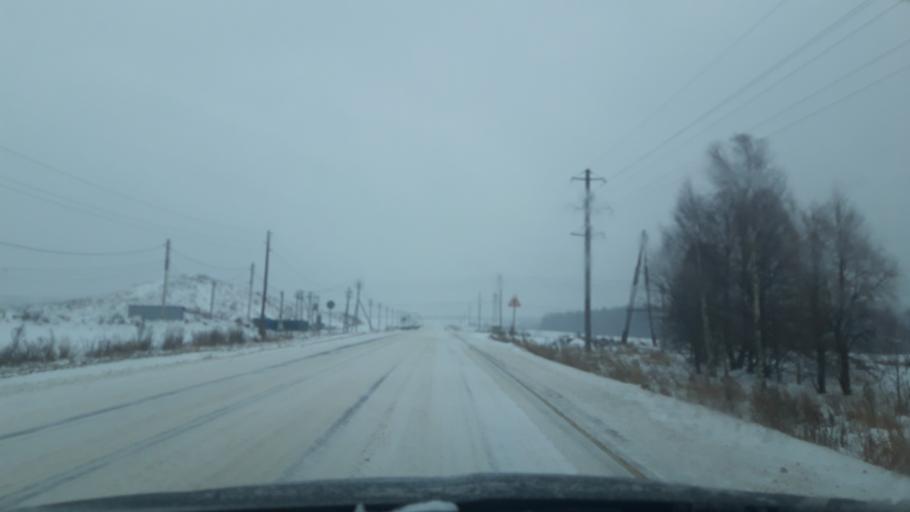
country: RU
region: Moskovskaya
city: Avtopoligon
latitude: 56.2608
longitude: 37.2273
